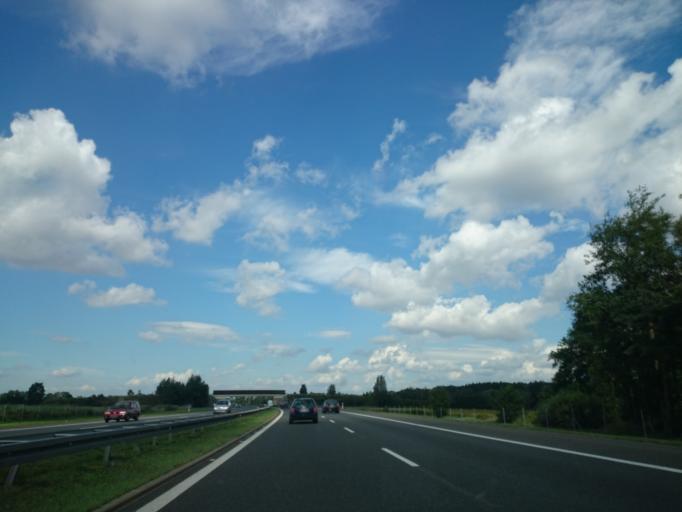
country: PL
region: Opole Voivodeship
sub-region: Powiat brzeski
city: Lewin Brzeski
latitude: 50.7047
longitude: 17.6145
